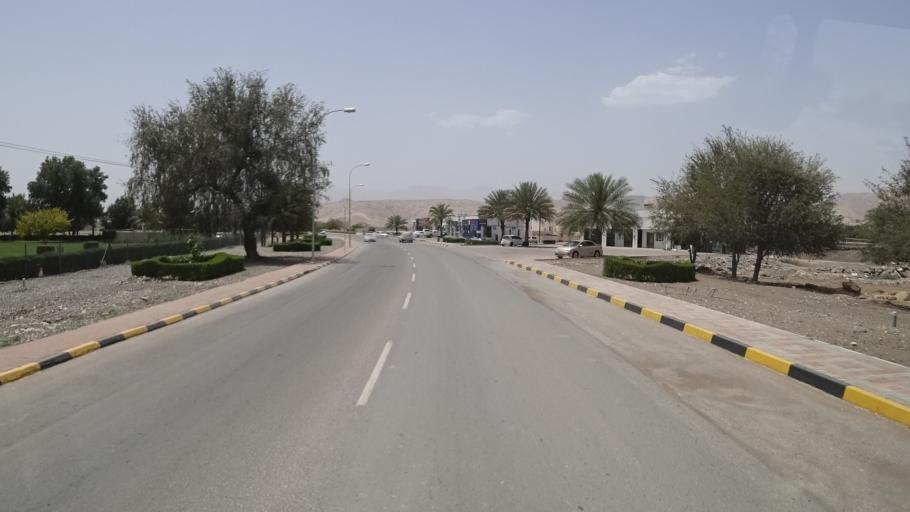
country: OM
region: Muhafazat Masqat
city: Muscat
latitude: 23.2568
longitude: 58.9114
